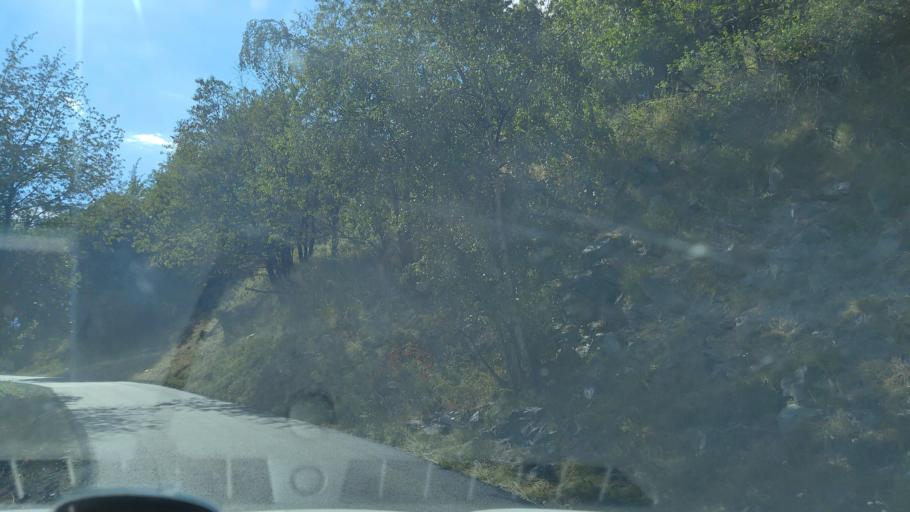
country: FR
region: Rhone-Alpes
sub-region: Departement de la Savoie
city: Val Thorens
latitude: 45.2193
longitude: 6.5579
